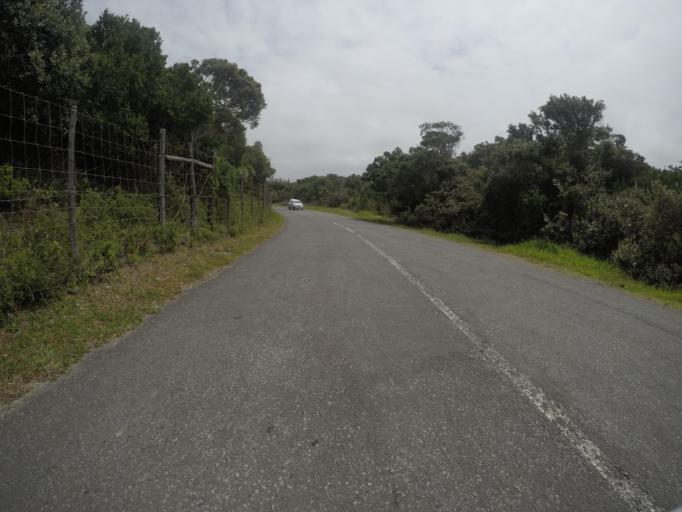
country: ZA
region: Eastern Cape
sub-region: Buffalo City Metropolitan Municipality
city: East London
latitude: -32.9930
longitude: 27.9453
